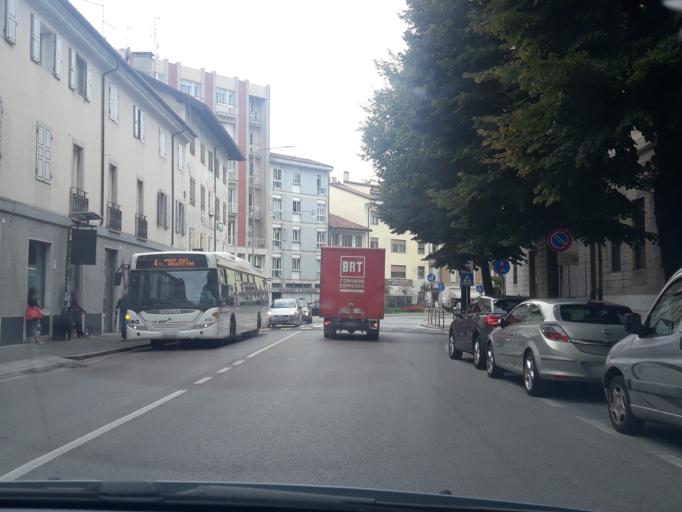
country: IT
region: Friuli Venezia Giulia
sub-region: Provincia di Udine
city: Udine
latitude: 46.0593
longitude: 13.2345
